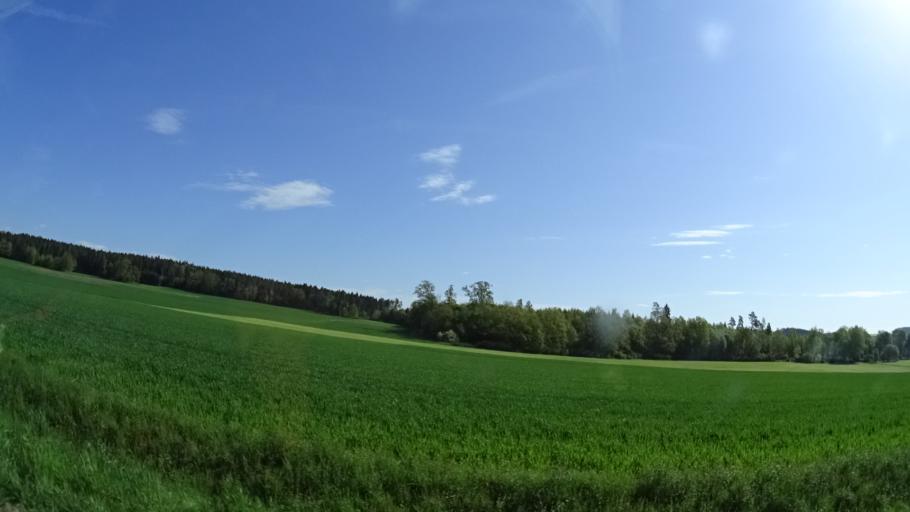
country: DE
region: Baden-Wuerttemberg
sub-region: Karlsruhe Region
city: Ebhausen
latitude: 48.5950
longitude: 8.6668
